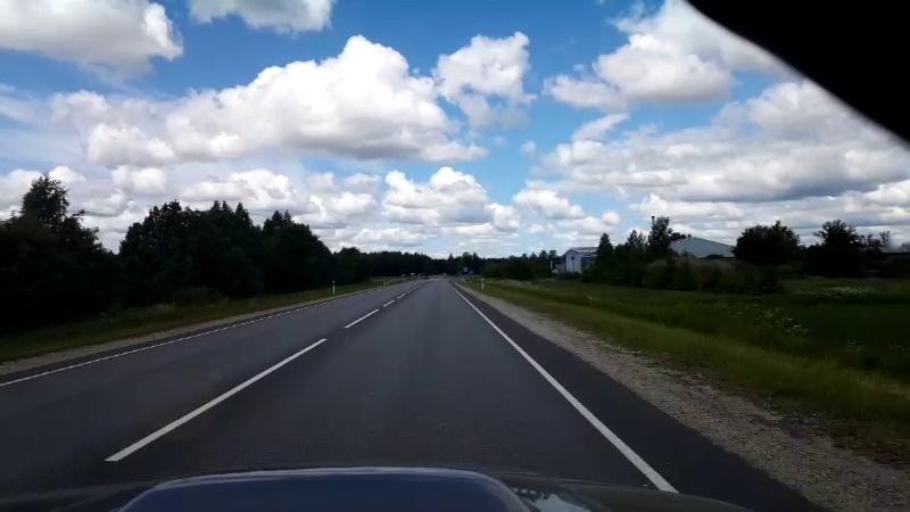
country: EE
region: Paernumaa
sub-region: Paikuse vald
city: Paikuse
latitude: 58.3138
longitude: 24.6035
